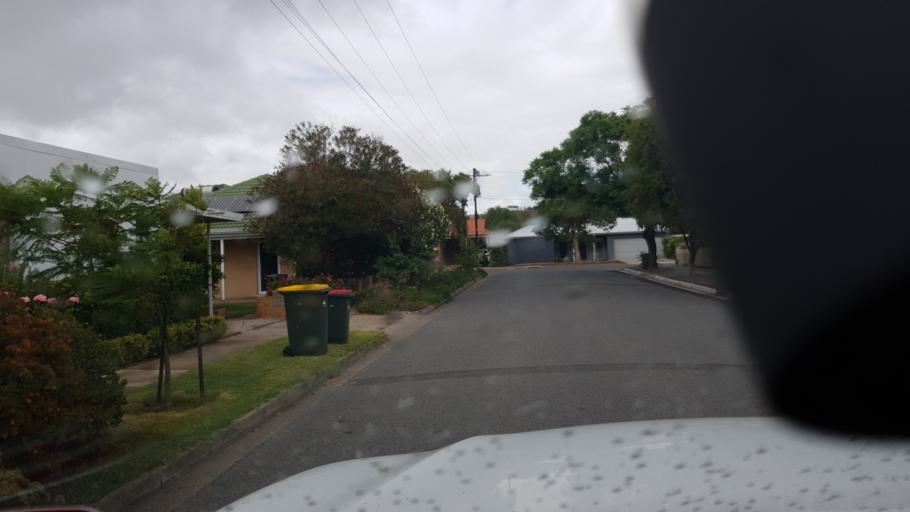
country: AU
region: South Australia
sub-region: Adelaide
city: Brighton
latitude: -35.0223
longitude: 138.5285
